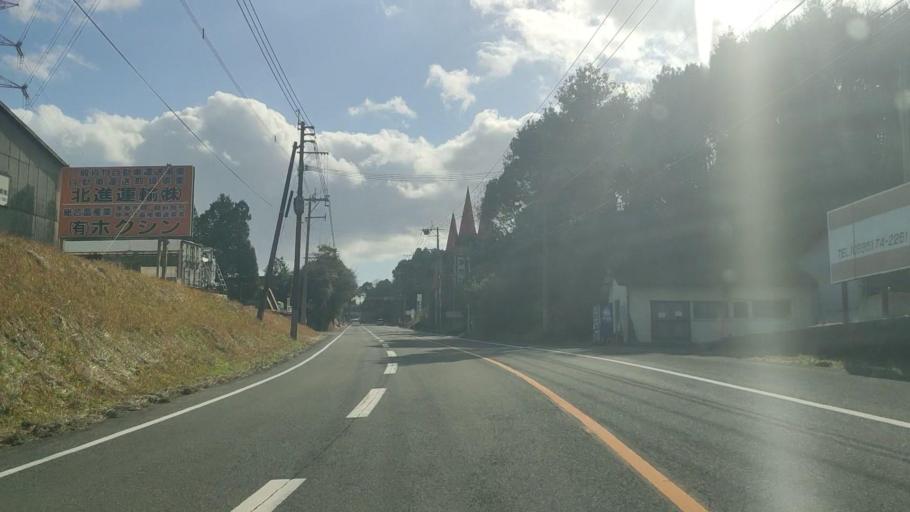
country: JP
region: Kagoshima
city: Okuchi-shinohara
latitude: 31.9319
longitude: 130.7029
